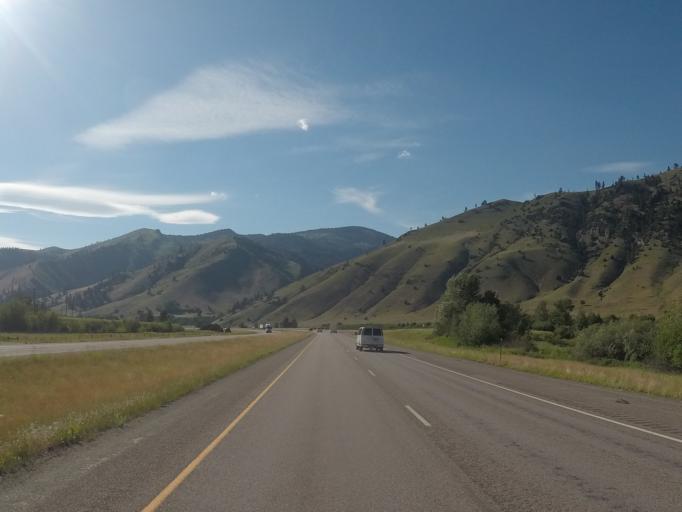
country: US
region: Montana
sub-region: Missoula County
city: Clinton
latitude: 46.7028
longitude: -113.3671
